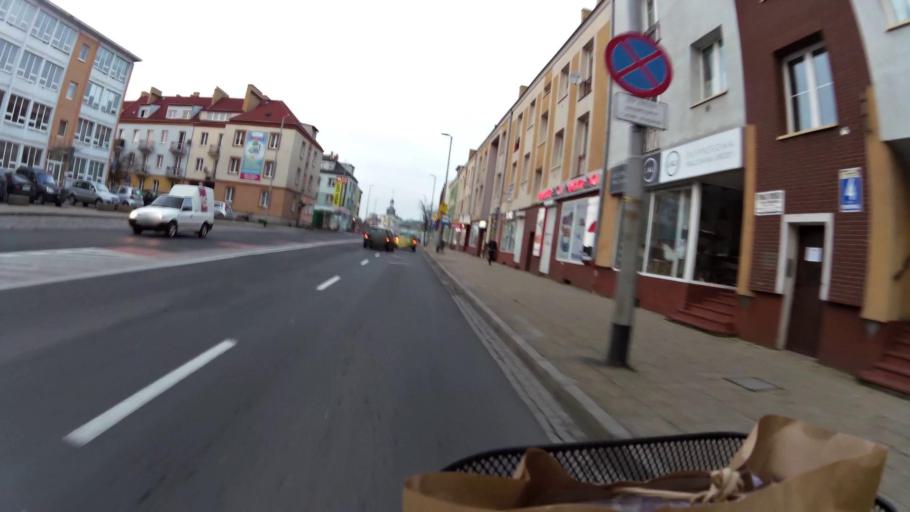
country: PL
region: West Pomeranian Voivodeship
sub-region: Koszalin
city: Koszalin
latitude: 54.1911
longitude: 16.1824
